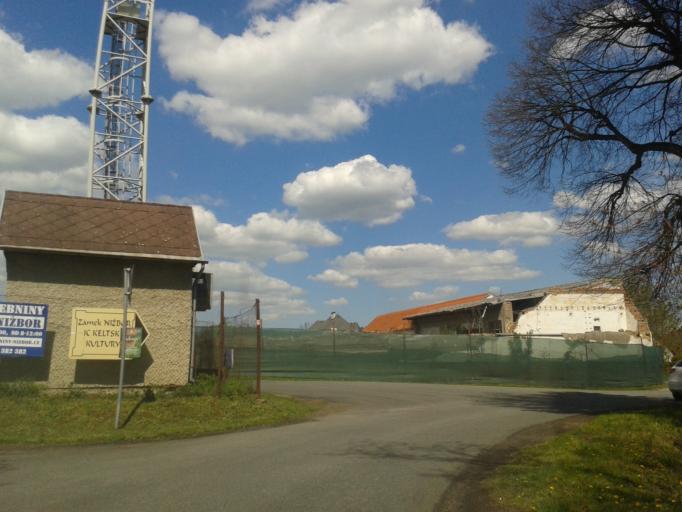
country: CZ
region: Central Bohemia
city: Nizbor
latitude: 49.9990
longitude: 13.9962
